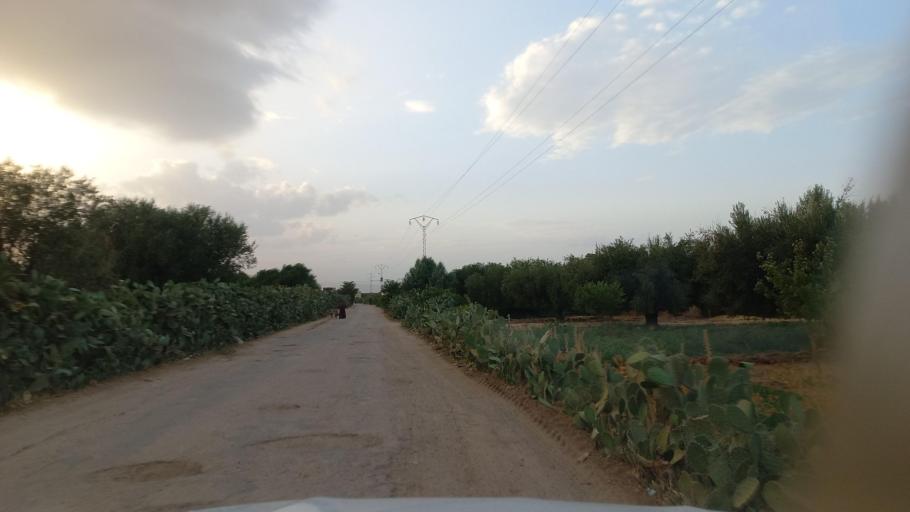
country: TN
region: Al Qasrayn
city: Kasserine
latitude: 35.2701
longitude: 9.0571
